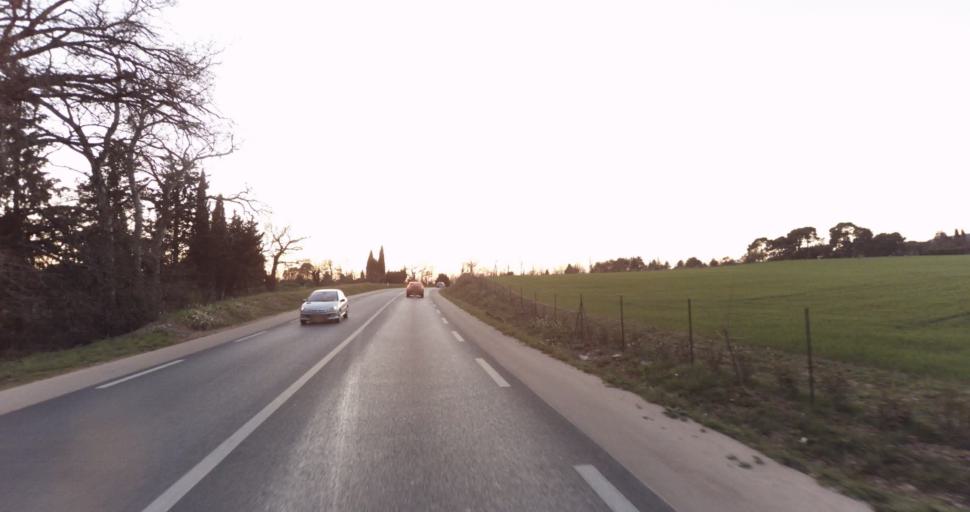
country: FR
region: Provence-Alpes-Cote d'Azur
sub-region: Departement des Bouches-du-Rhone
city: Eguilles
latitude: 43.5374
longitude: 5.3837
